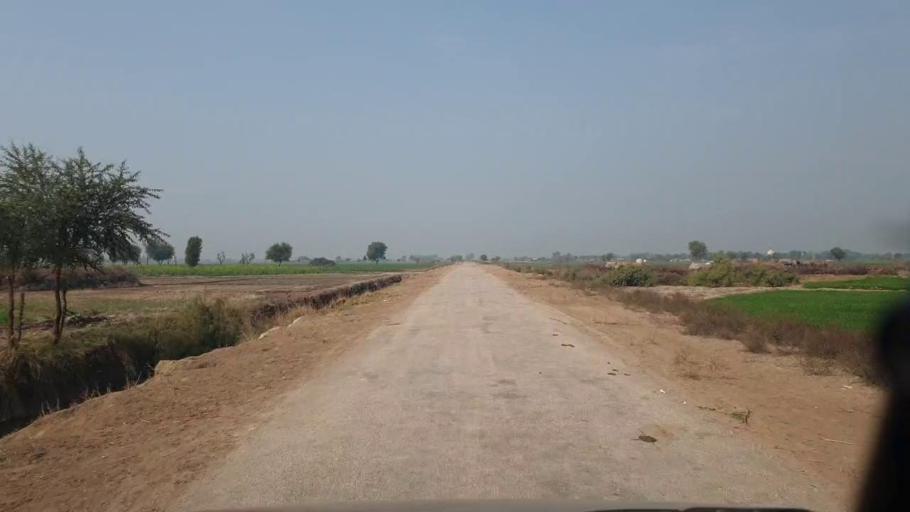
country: PK
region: Sindh
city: Shahdadpur
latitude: 26.0225
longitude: 68.5365
